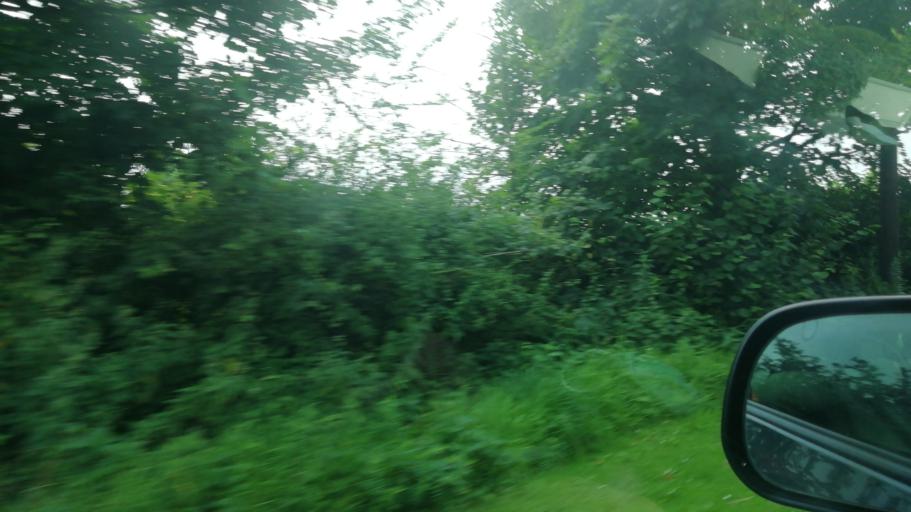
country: IE
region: Munster
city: Fethard
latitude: 52.5852
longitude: -7.5954
